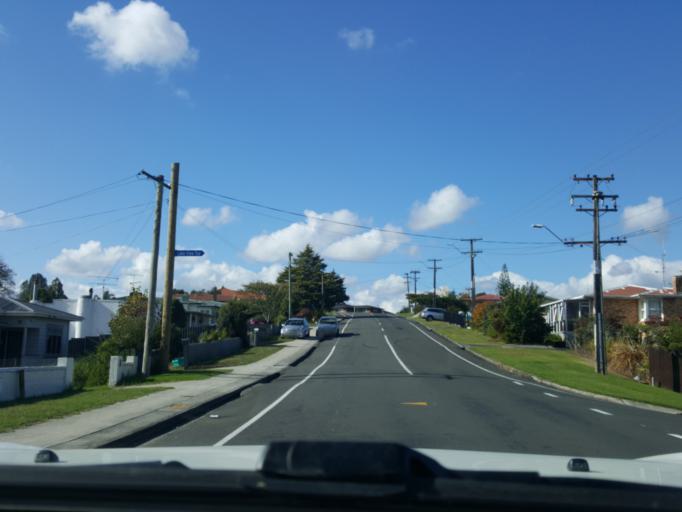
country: NZ
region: Waikato
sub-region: Waikato District
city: Ngaruawahia
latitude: -37.5475
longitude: 175.1661
